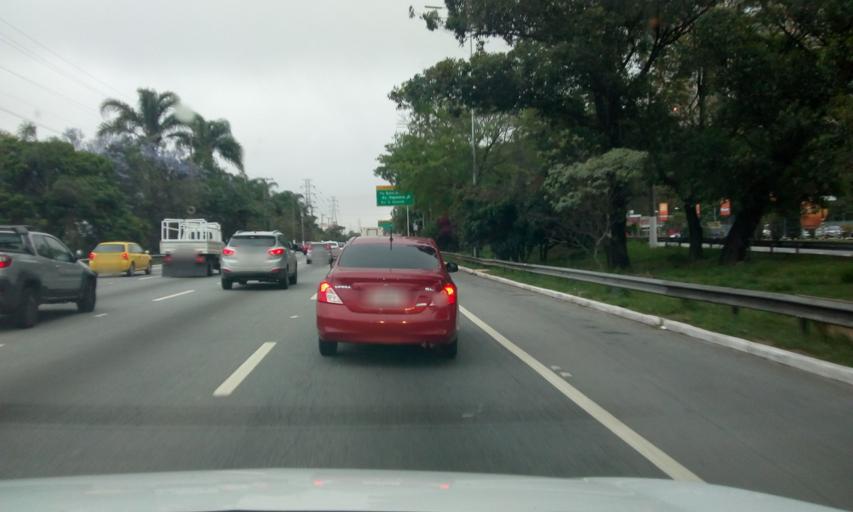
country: BR
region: Sao Paulo
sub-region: Taboao Da Serra
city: Taboao da Serra
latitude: -23.6295
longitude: -46.7162
